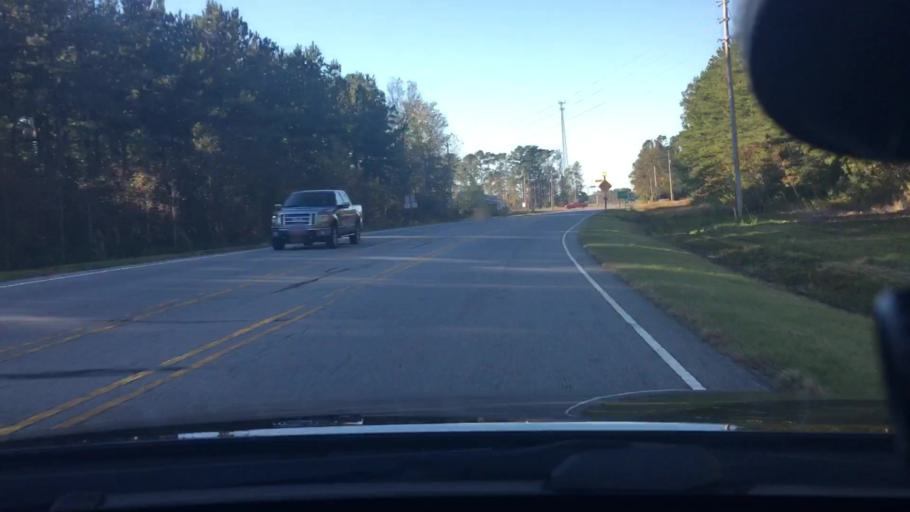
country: US
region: North Carolina
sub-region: Craven County
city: Vanceboro
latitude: 35.4167
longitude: -77.2550
